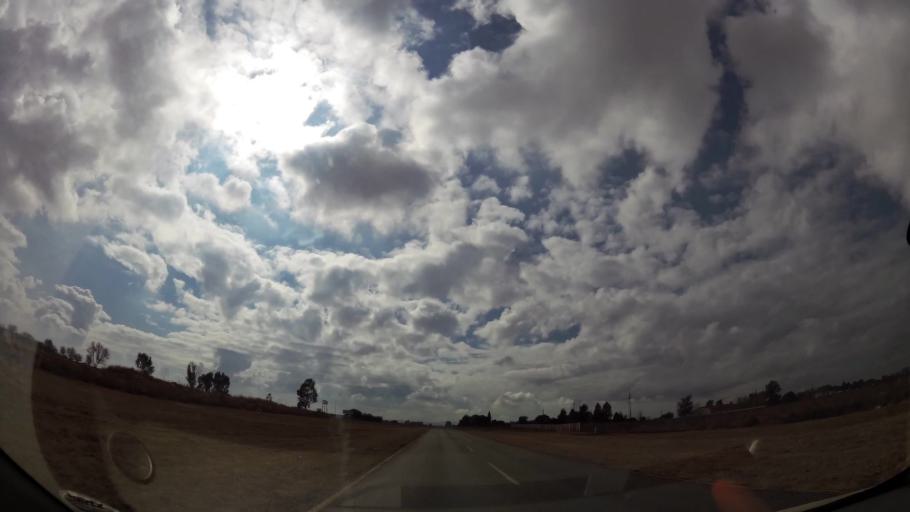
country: ZA
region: Gauteng
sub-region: Sedibeng District Municipality
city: Meyerton
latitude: -26.6170
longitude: 28.0602
